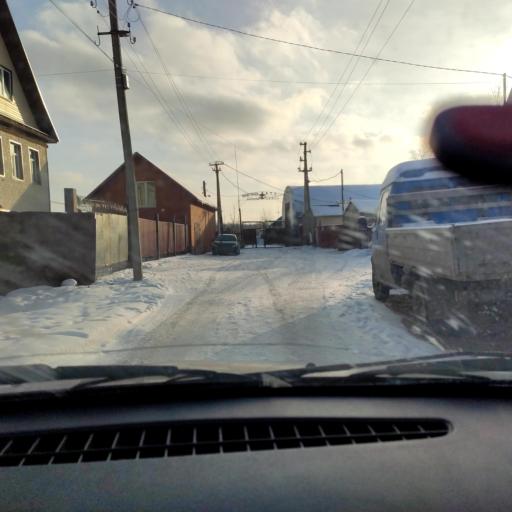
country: RU
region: Bashkortostan
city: Ufa
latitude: 54.6904
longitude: 55.9461
